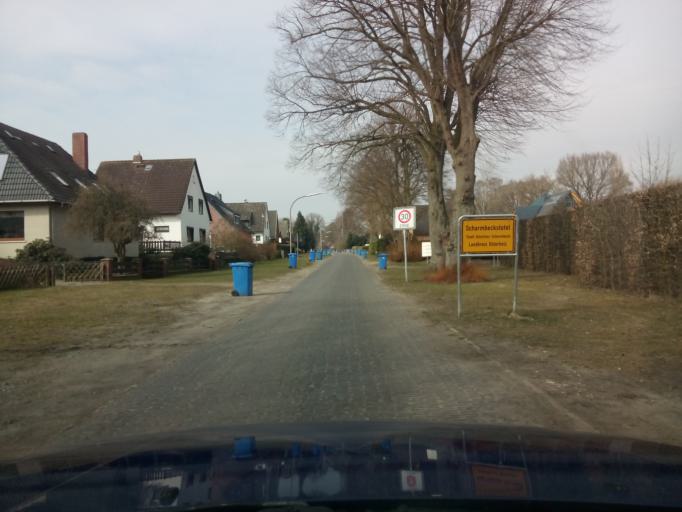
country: DE
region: Lower Saxony
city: Ritterhude
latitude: 53.1988
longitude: 8.7683
